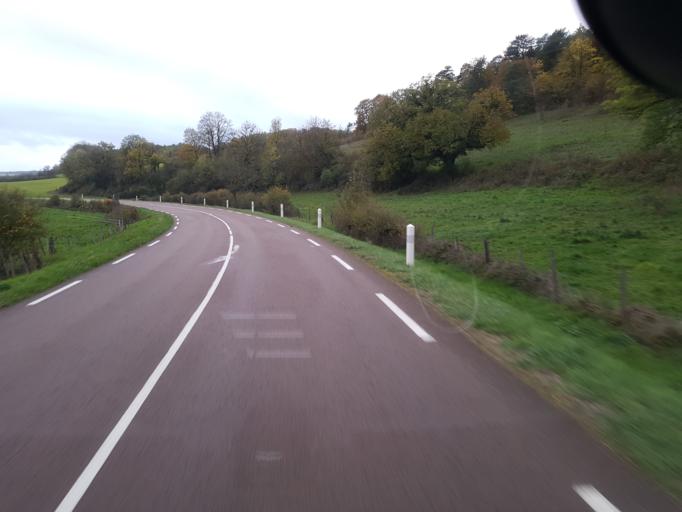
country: FR
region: Bourgogne
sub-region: Departement de la Cote-d'Or
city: Chatillon-sur-Seine
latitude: 47.6807
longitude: 4.7023
